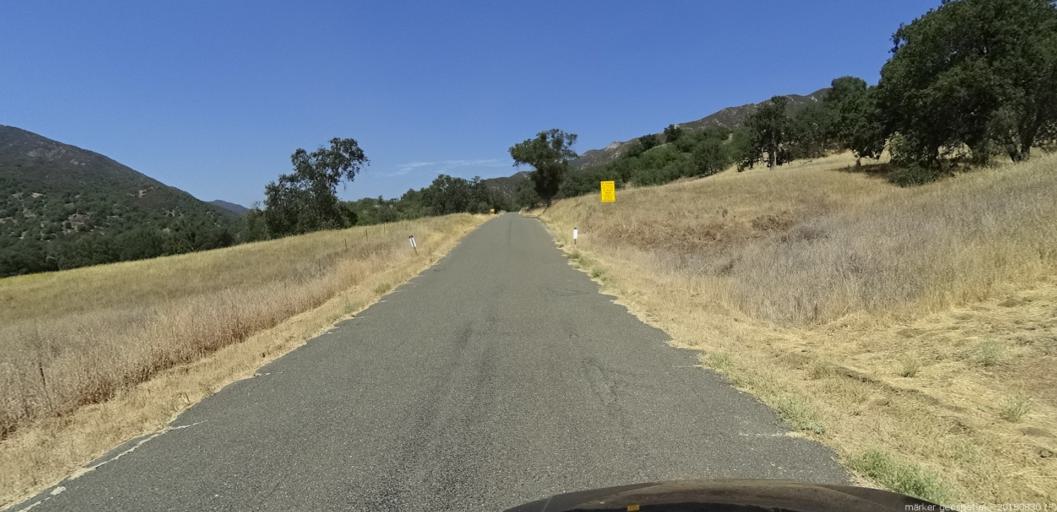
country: US
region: California
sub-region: Monterey County
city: King City
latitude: 35.9836
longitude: -121.3500
